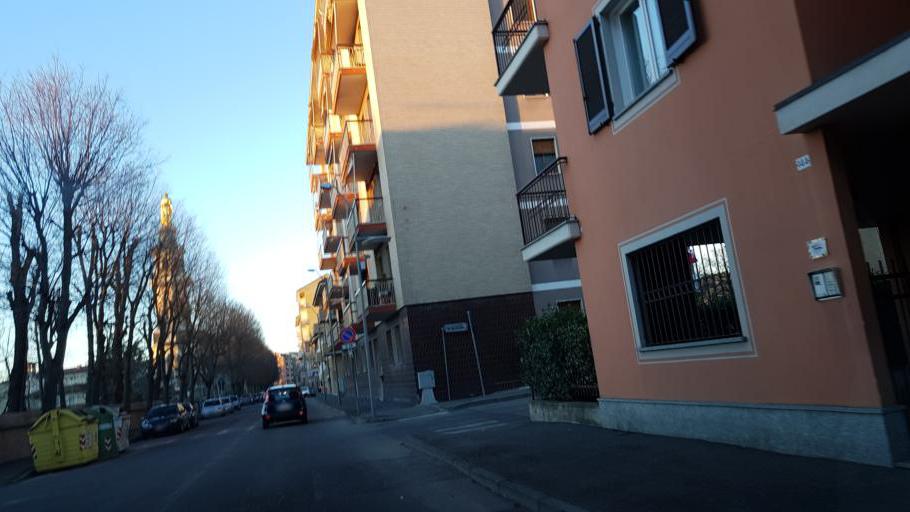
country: IT
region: Piedmont
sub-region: Provincia di Alessandria
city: Tortona
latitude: 44.8857
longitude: 8.8591
